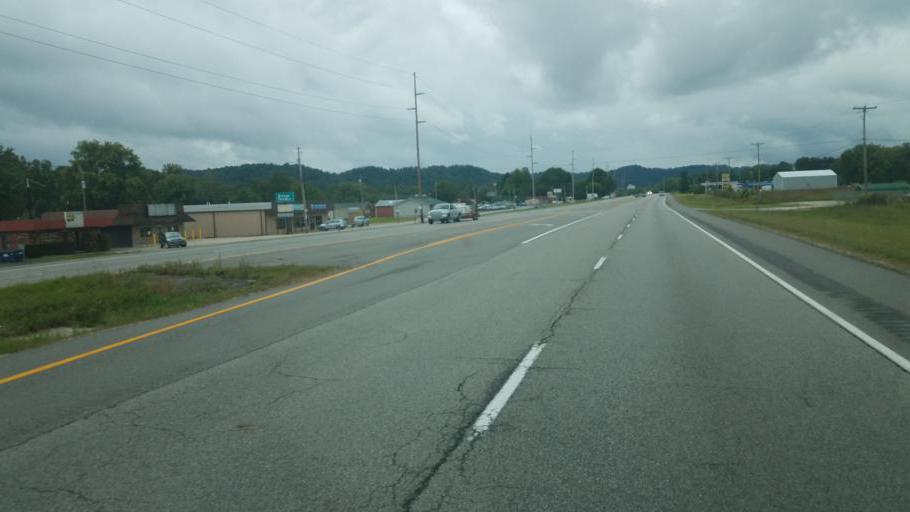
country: US
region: Ohio
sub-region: Scioto County
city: New Boston
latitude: 38.7287
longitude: -82.9314
